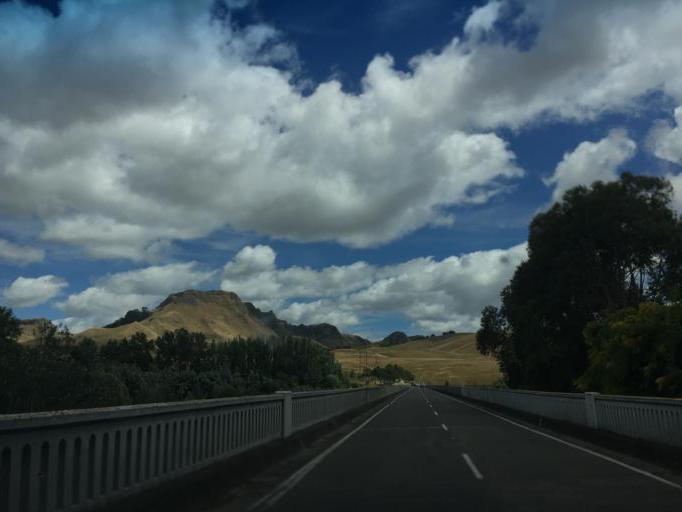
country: NZ
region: Hawke's Bay
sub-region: Hastings District
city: Hastings
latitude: -39.7172
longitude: 176.9291
